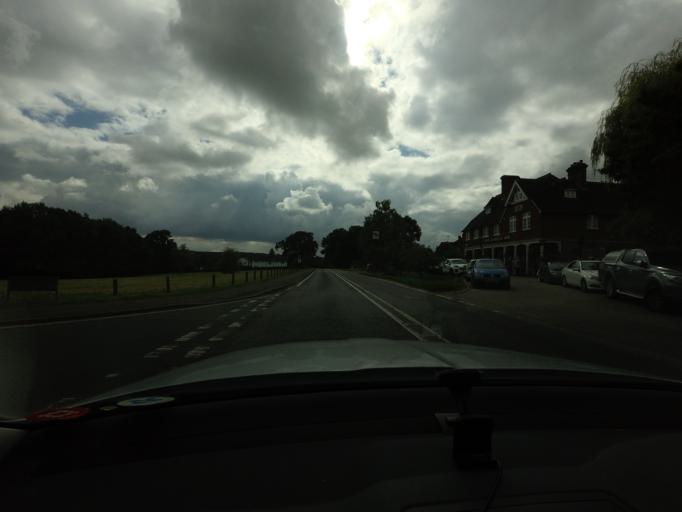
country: GB
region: England
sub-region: Kent
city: Borough Green
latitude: 51.2469
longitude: 0.2798
